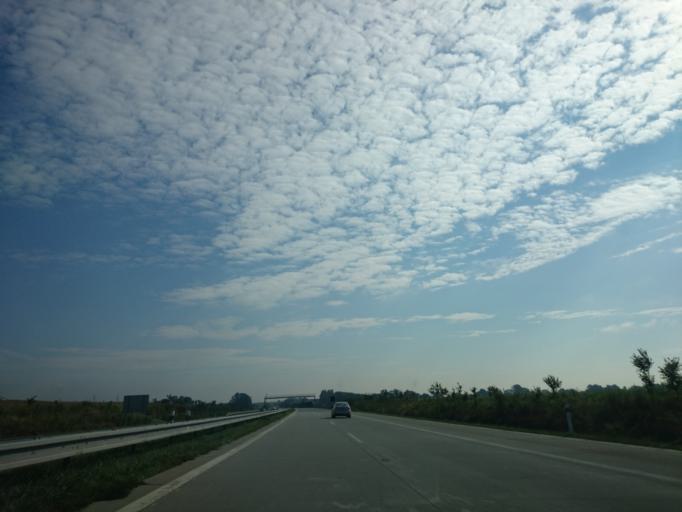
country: CZ
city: Kunin
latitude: 49.6952
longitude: 17.9704
